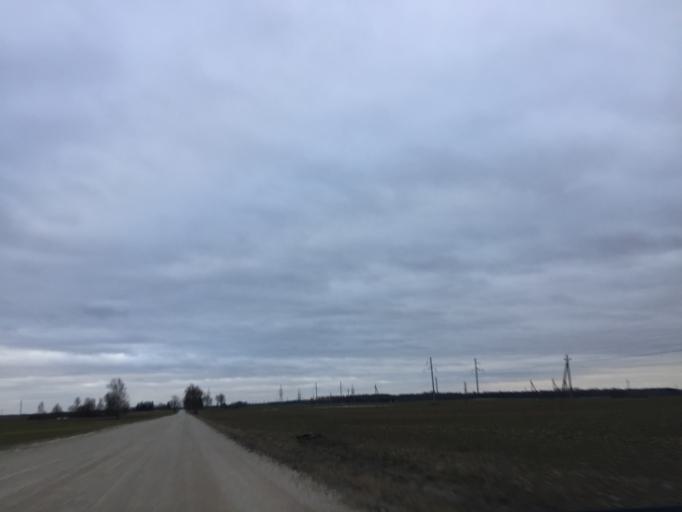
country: LT
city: Zagare
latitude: 56.3434
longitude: 23.2505
